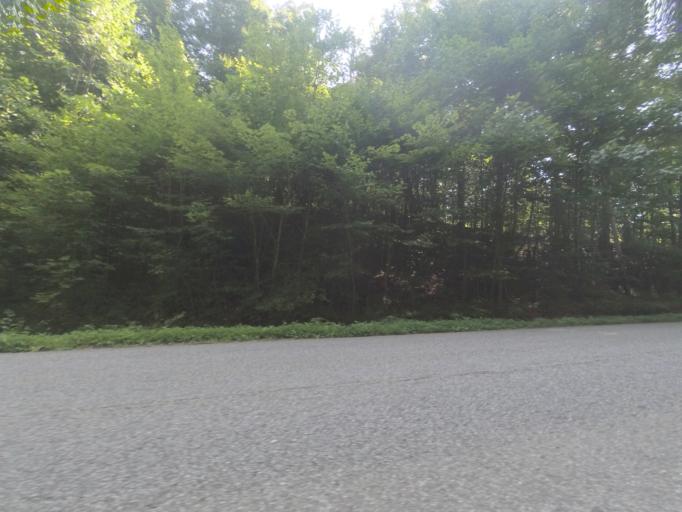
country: US
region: West Virginia
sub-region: Cabell County
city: Huntington
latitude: 38.4372
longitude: -82.4326
